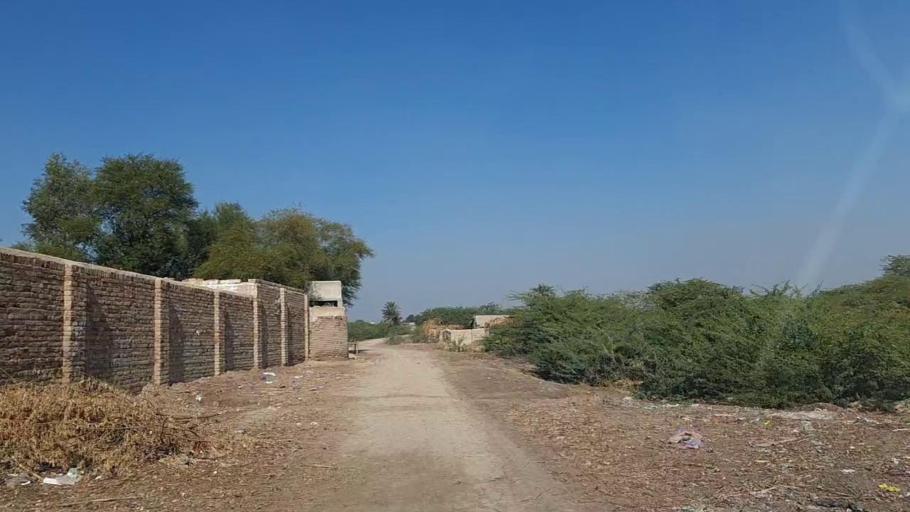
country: PK
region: Sindh
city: Nawabshah
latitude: 26.3390
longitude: 68.3545
